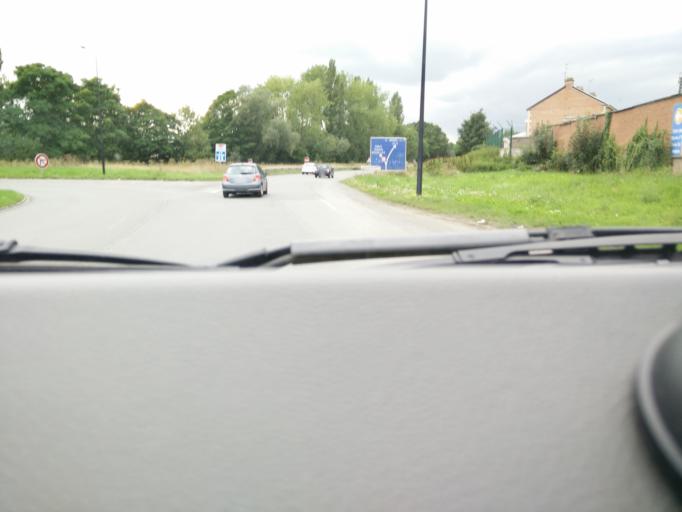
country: FR
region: Nord-Pas-de-Calais
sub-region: Departement du Nord
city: La Sentinelle
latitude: 50.3565
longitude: 3.4922
